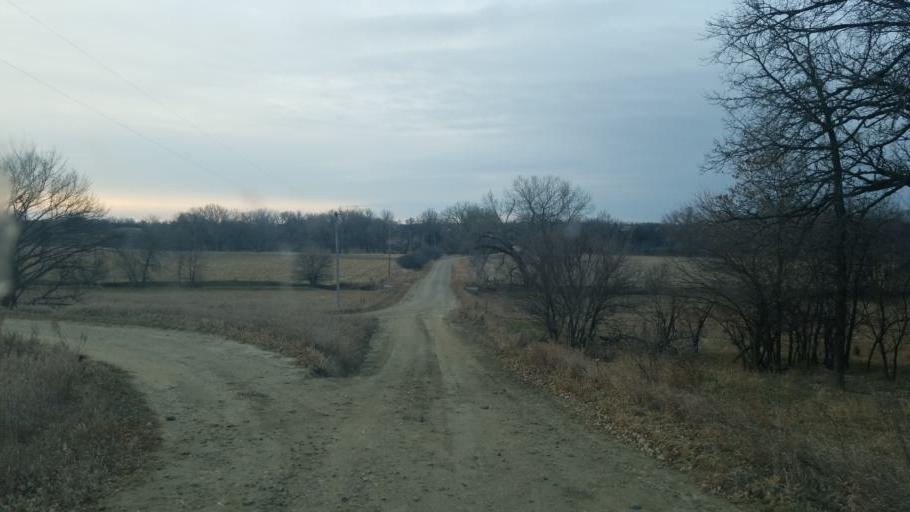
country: US
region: Nebraska
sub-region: Knox County
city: Center
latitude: 42.5583
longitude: -97.7986
